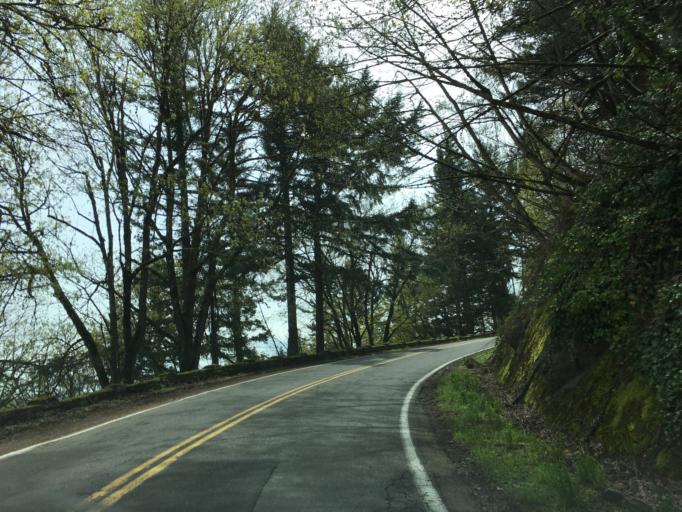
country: US
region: Oregon
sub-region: Multnomah County
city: Lents
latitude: 45.5470
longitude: -122.5647
